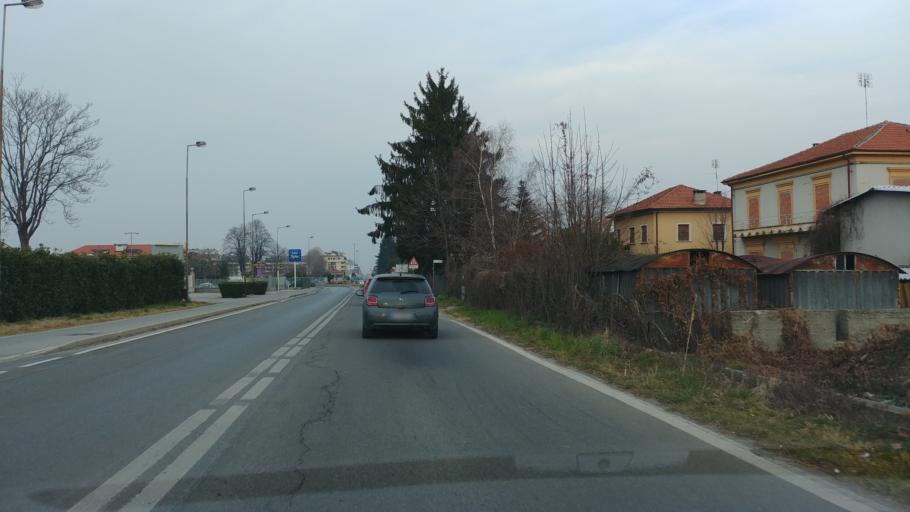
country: IT
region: Piedmont
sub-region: Provincia di Cuneo
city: Cuneo
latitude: 44.3705
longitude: 7.5283
